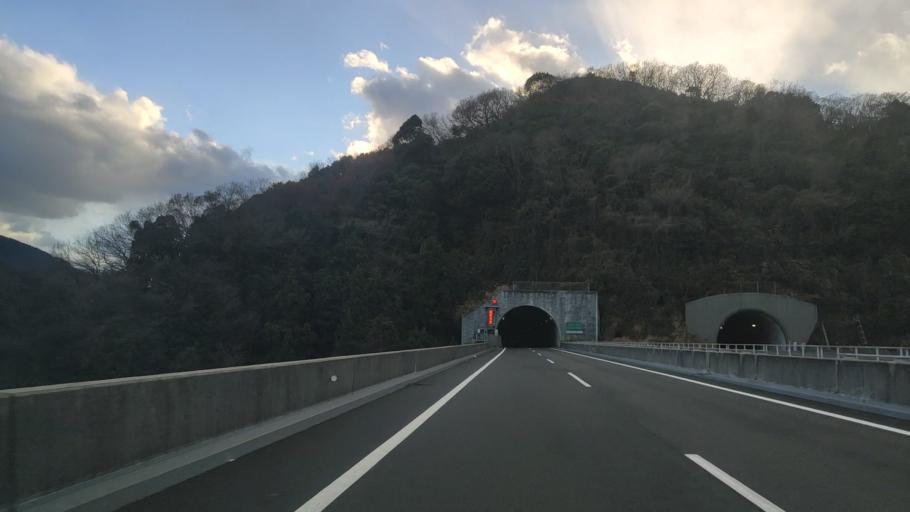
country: JP
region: Ehime
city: Saijo
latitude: 33.8454
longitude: 132.9933
